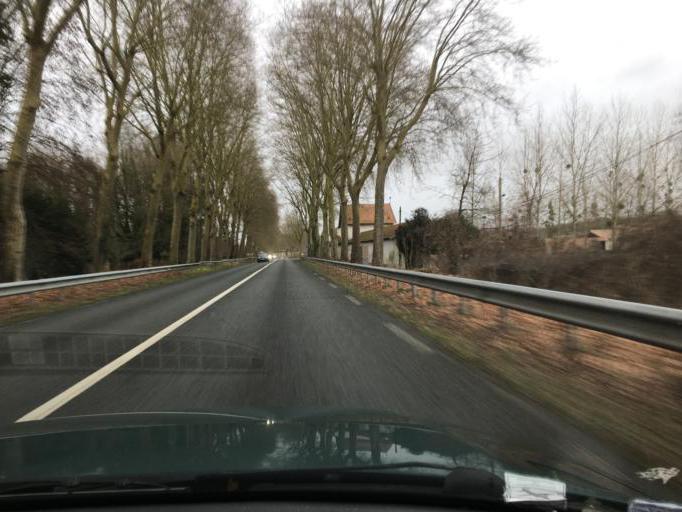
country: FR
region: Picardie
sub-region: Departement de l'Oise
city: La Chapelle-en-Serval
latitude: 49.1422
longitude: 2.5400
